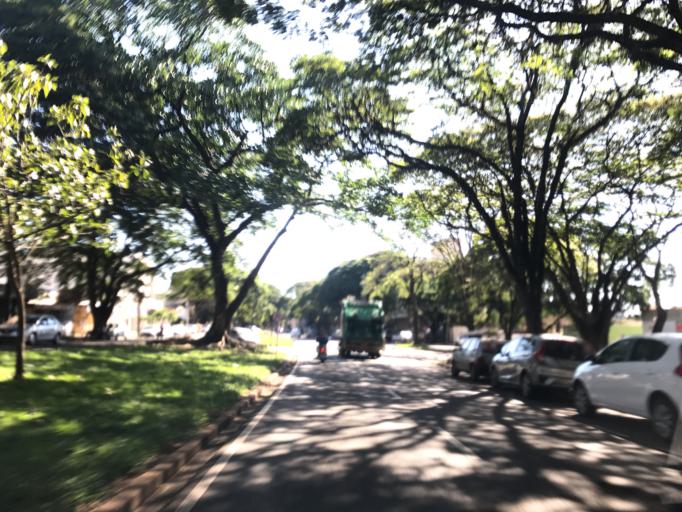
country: BR
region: Parana
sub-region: Maringa
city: Maringa
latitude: -23.4294
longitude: -51.9522
